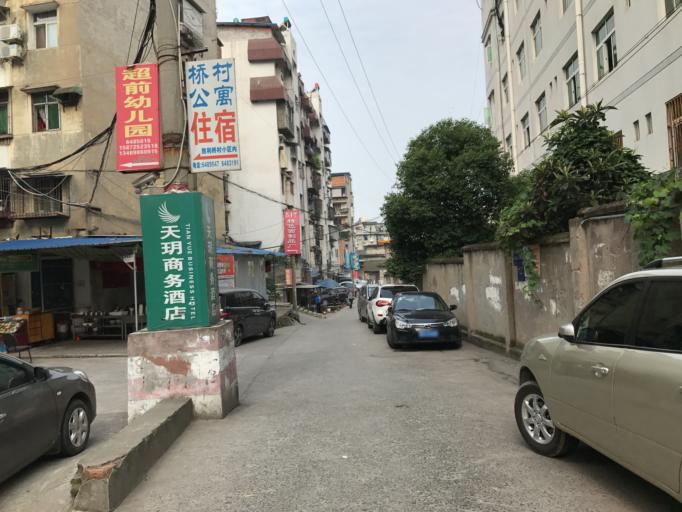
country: CN
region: Hubei
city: Yaowan
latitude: 30.6930
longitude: 111.2965
